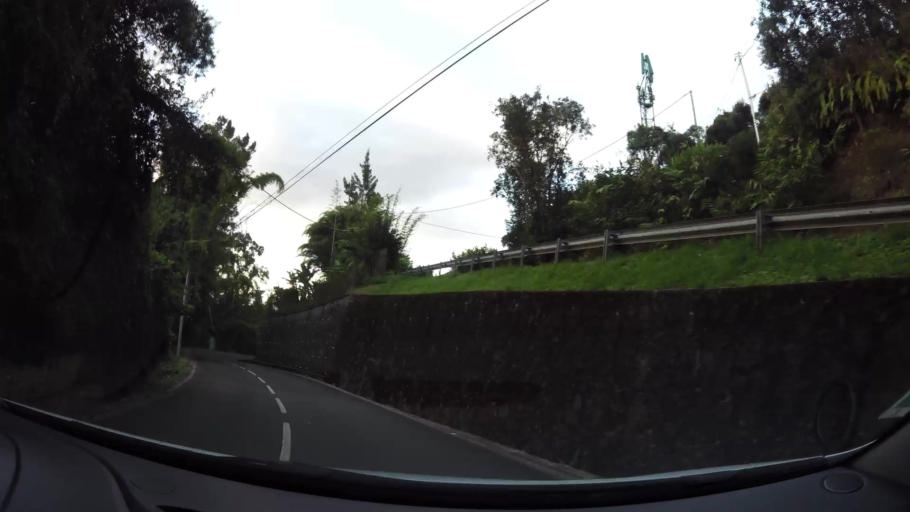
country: RE
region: Reunion
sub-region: Reunion
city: Saint-Denis
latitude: -20.9226
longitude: 55.4497
